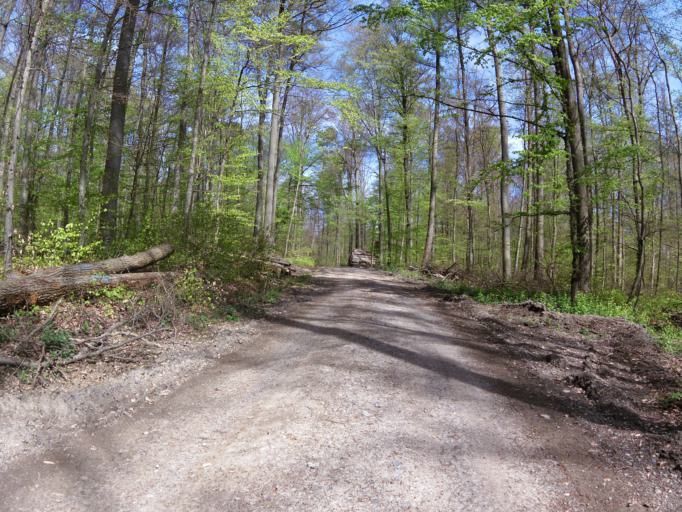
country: DE
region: Bavaria
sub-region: Regierungsbezirk Unterfranken
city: Rimpar
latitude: 49.8612
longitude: 9.9843
